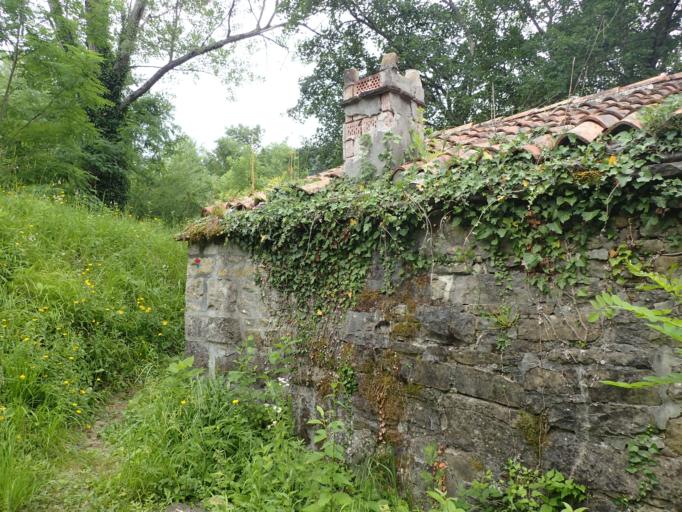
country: SI
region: Koper-Capodistria
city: Sv. Anton
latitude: 45.4772
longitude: 13.8348
